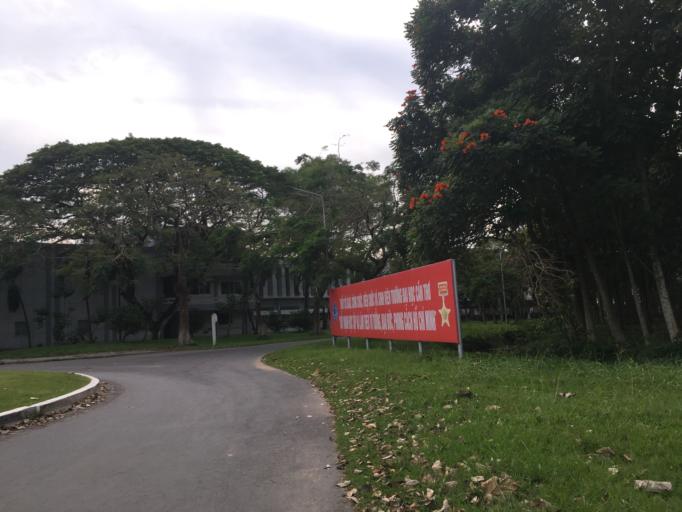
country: VN
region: Can Tho
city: Can Tho
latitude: 10.0314
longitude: 105.7709
